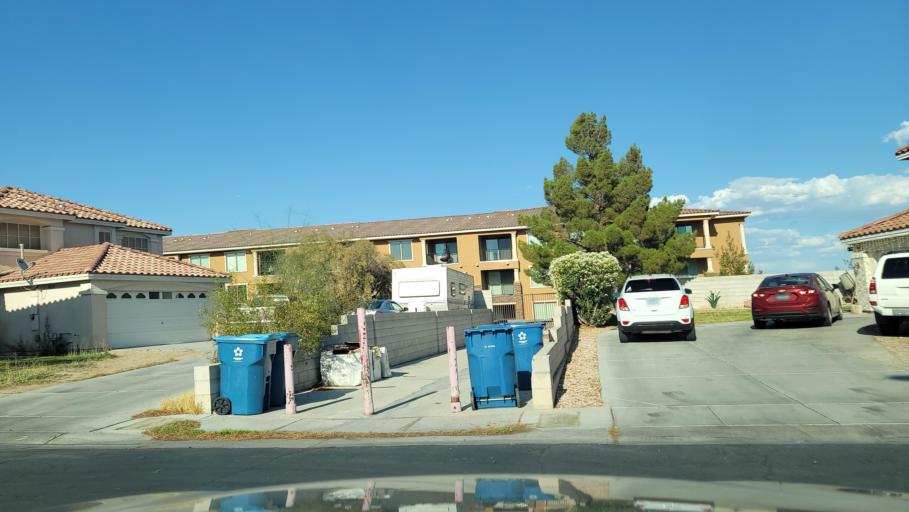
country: US
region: Nevada
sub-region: Clark County
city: Summerlin South
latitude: 36.0931
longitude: -115.3001
